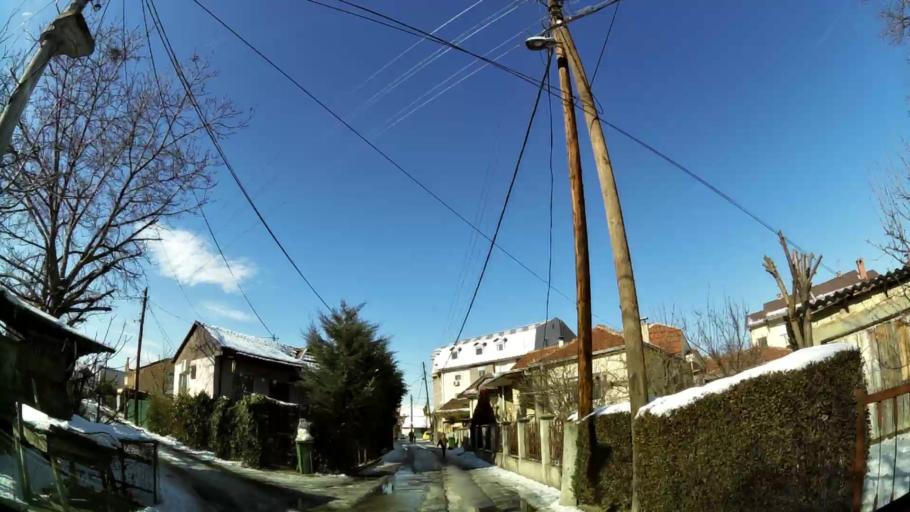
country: MK
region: Saraj
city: Saraj
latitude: 42.0092
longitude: 21.3474
